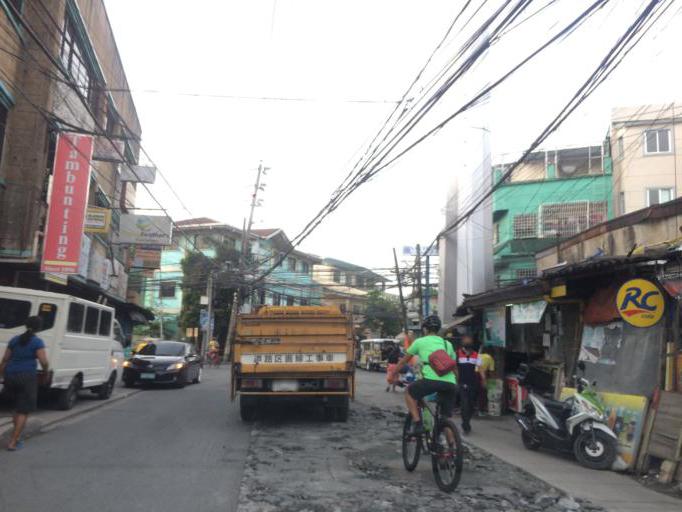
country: PH
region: Calabarzon
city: Del Monte
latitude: 14.6558
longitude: 121.0114
